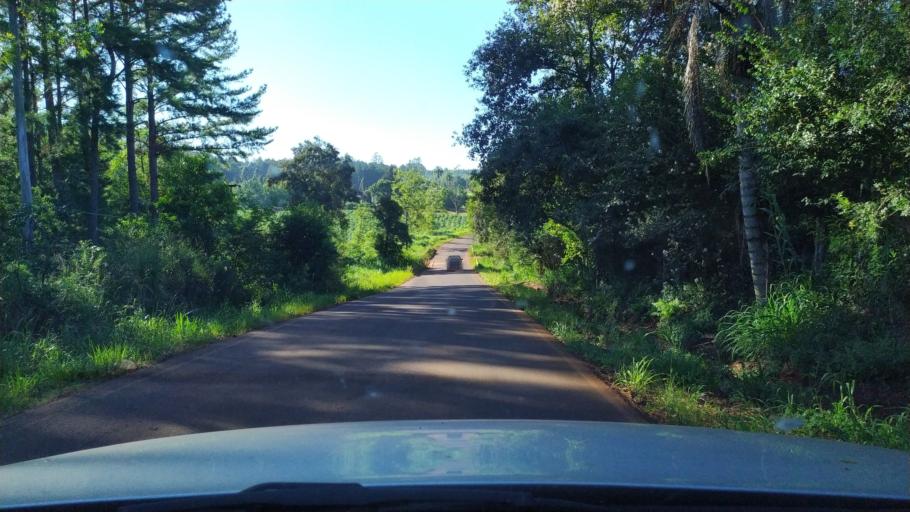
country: AR
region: Misiones
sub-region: Departamento de Montecarlo
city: Montecarlo
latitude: -26.5968
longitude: -54.7047
